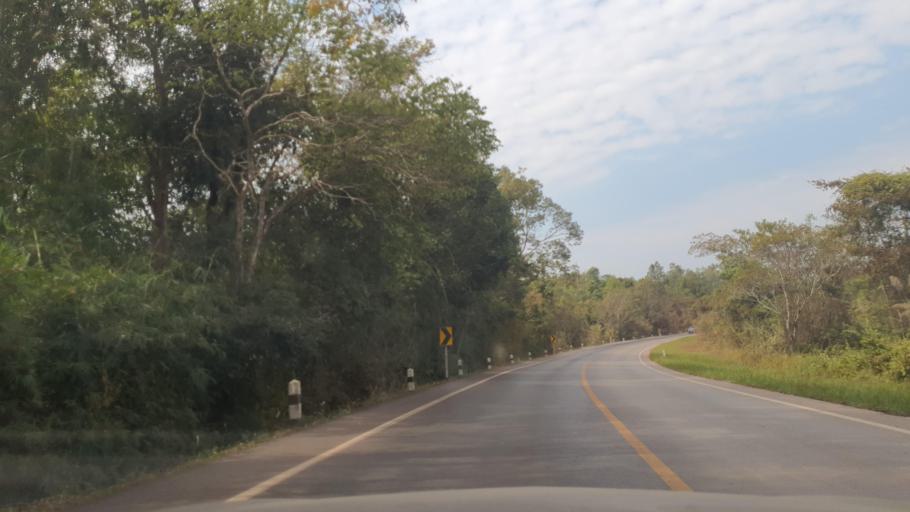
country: TH
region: Changwat Bueng Kan
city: Bung Khla
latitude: 18.2869
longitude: 103.8955
